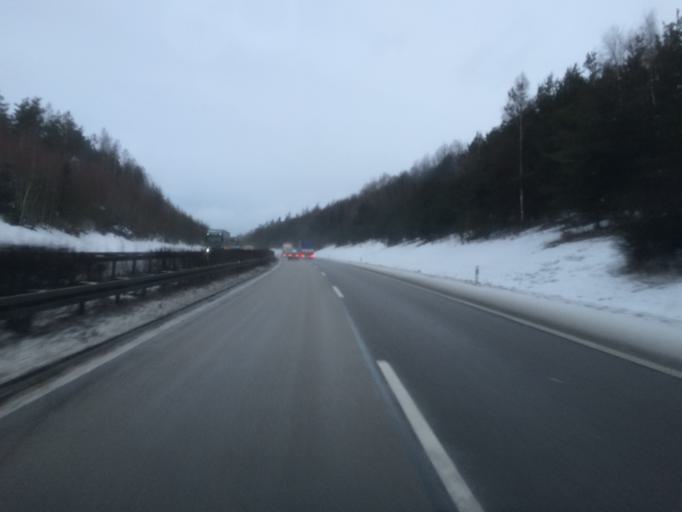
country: DE
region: Bavaria
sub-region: Upper Palatinate
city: Zeitlarn
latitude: 49.0822
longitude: 12.1009
